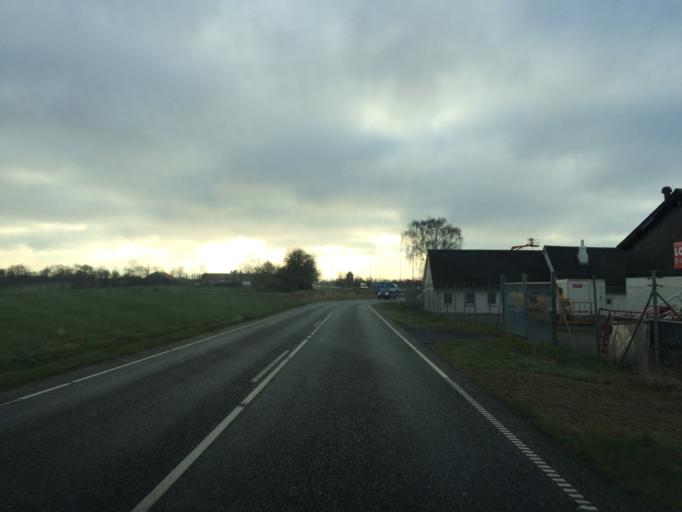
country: DK
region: South Denmark
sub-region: Fredericia Kommune
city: Snoghoj
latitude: 55.5684
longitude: 9.6877
